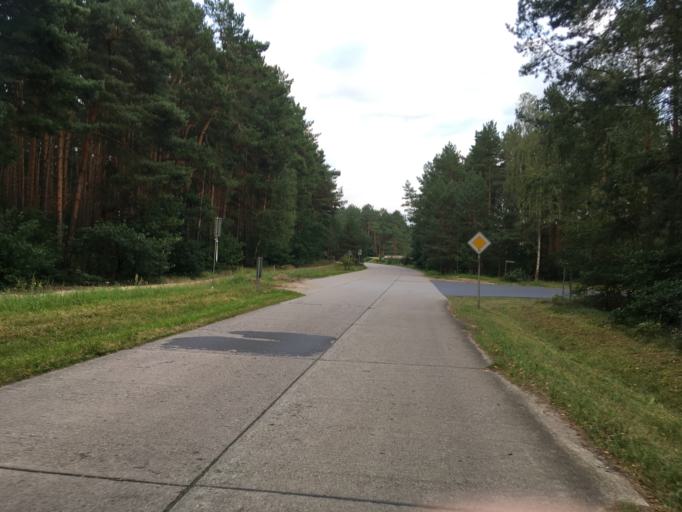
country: DE
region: Brandenburg
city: Grunheide
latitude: 52.3820
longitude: 13.7952
